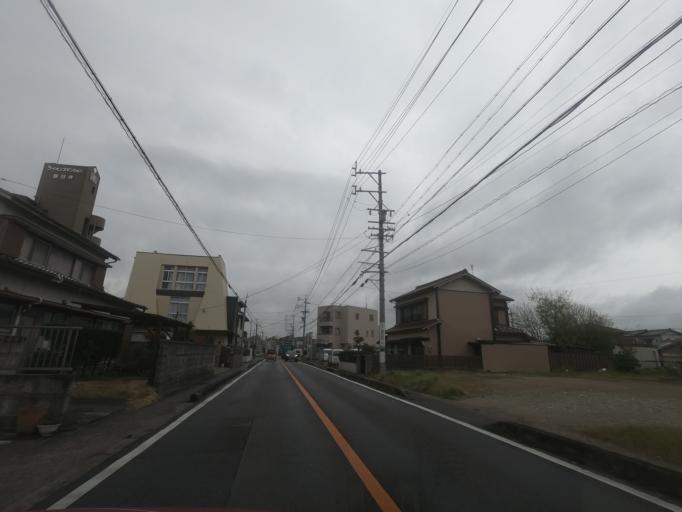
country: JP
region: Aichi
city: Kasugai
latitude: 35.2486
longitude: 136.9897
